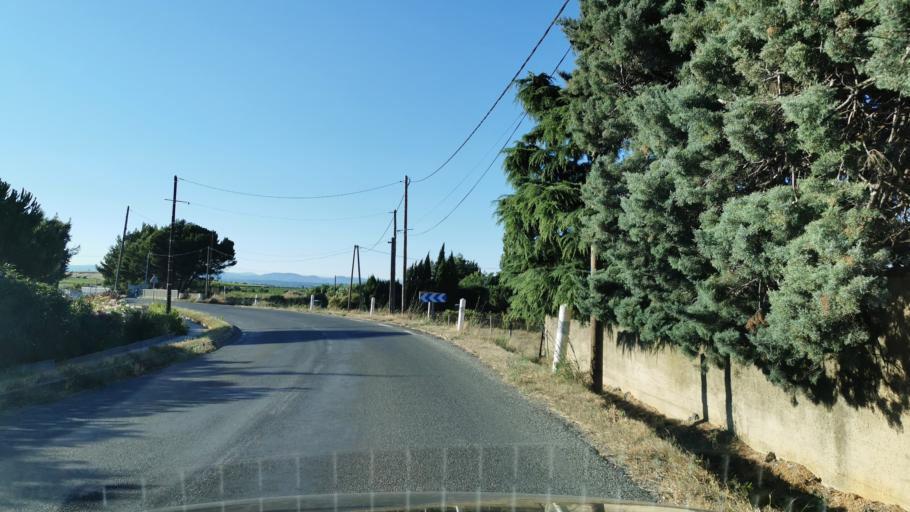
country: FR
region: Languedoc-Roussillon
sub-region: Departement de l'Aude
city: Ouveillan
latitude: 43.2680
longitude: 2.9951
